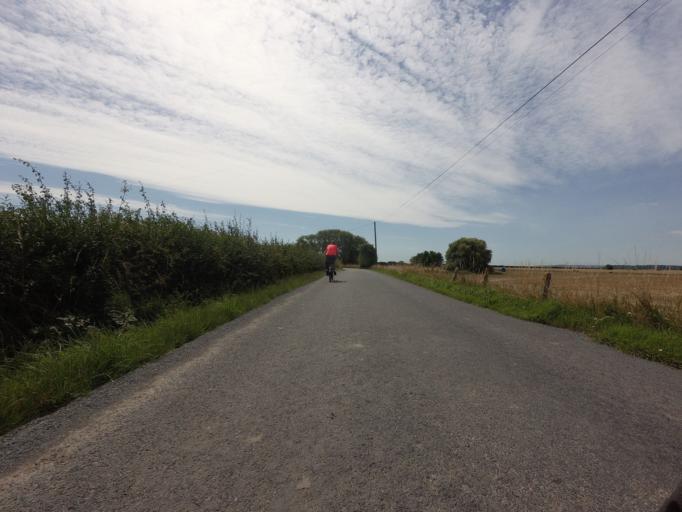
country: GB
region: England
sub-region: Kent
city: Stone
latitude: 50.9986
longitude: 0.8031
